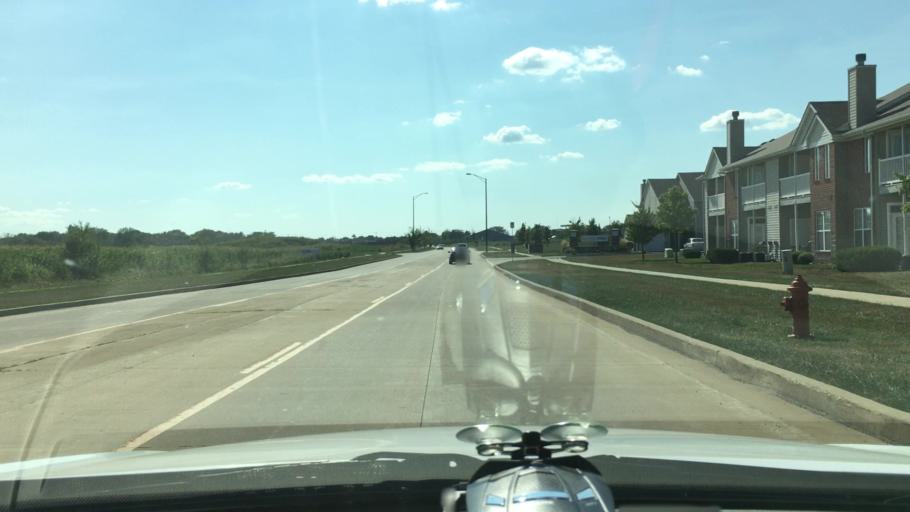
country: US
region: Illinois
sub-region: Champaign County
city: Champaign
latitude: 40.1491
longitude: -88.2601
